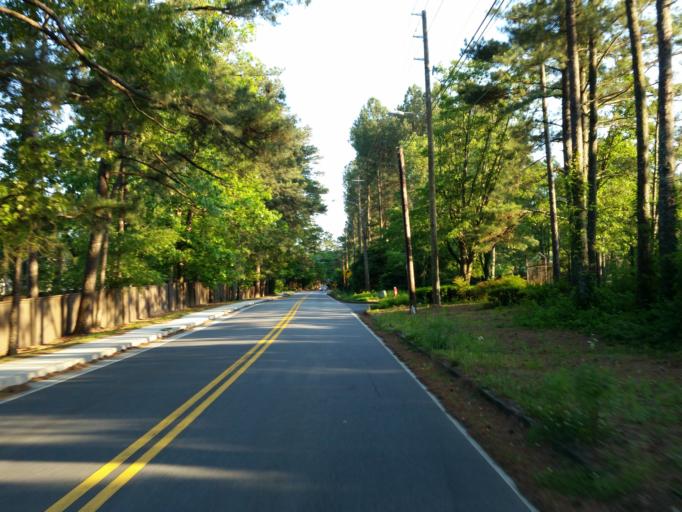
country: US
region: Georgia
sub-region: Cobb County
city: Smyrna
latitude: 33.9369
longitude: -84.4808
